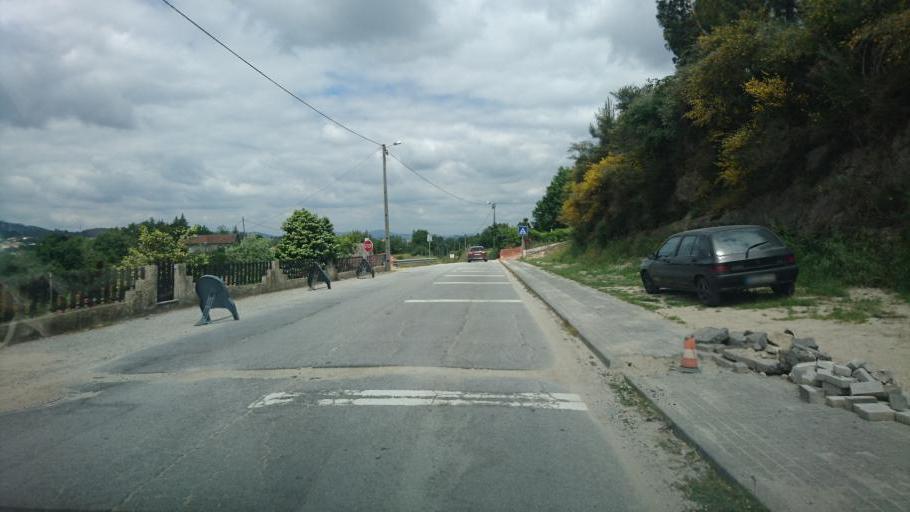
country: PT
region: Porto
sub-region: Paredes
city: Baltar
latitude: 41.1604
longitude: -8.3573
